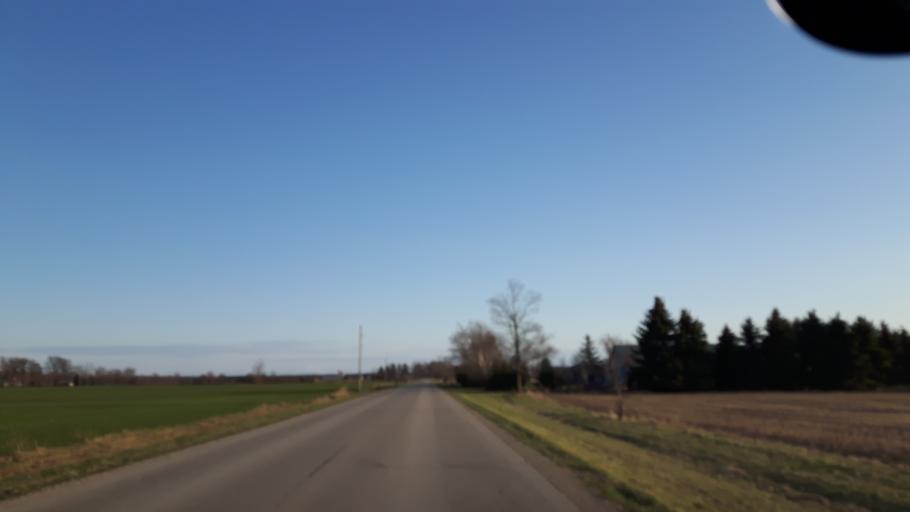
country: CA
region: Ontario
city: Goderich
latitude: 43.6487
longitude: -81.6846
